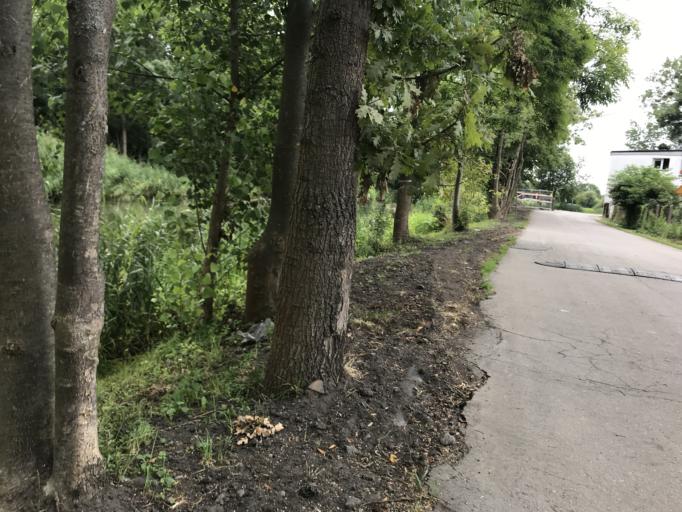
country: PL
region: Warmian-Masurian Voivodeship
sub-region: Powiat elblaski
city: Elblag
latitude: 54.1572
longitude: 19.3865
